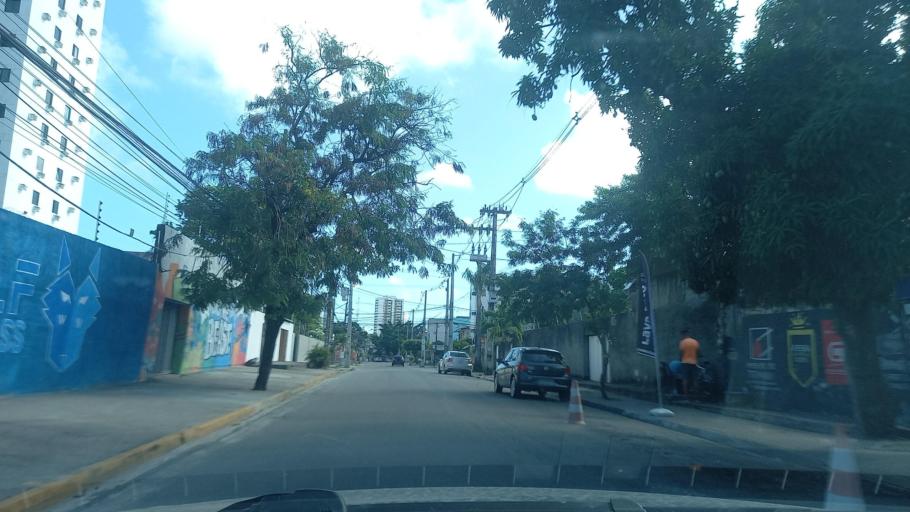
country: BR
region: Pernambuco
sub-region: Jaboatao Dos Guararapes
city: Jaboatao
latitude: -8.1940
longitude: -34.9222
